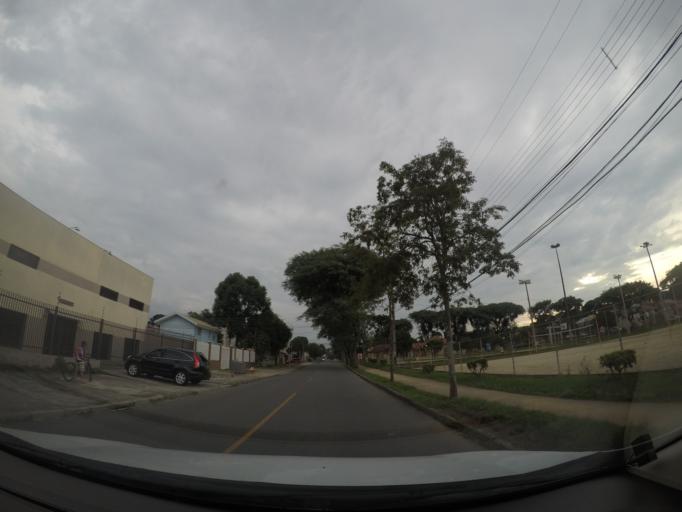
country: BR
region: Parana
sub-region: Sao Jose Dos Pinhais
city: Sao Jose dos Pinhais
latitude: -25.5178
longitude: -49.2351
